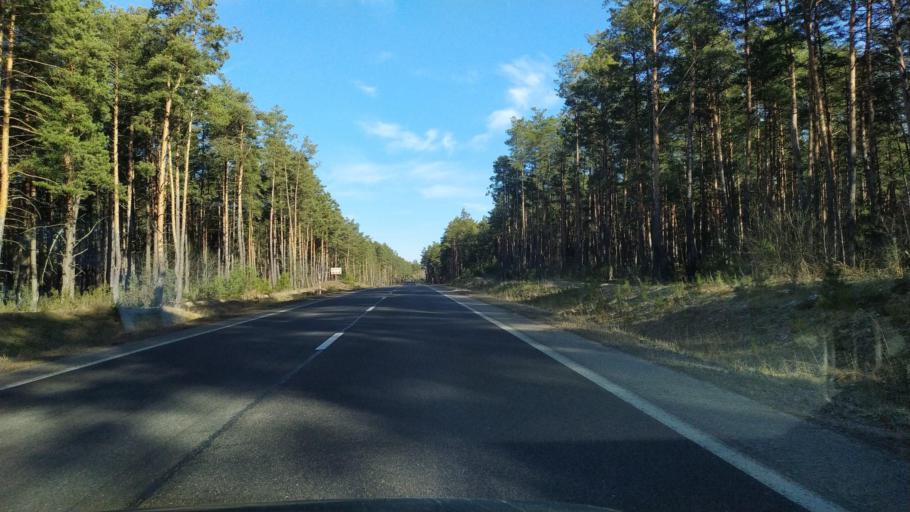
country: BY
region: Brest
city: Zhabinka
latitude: 52.4331
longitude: 24.1267
